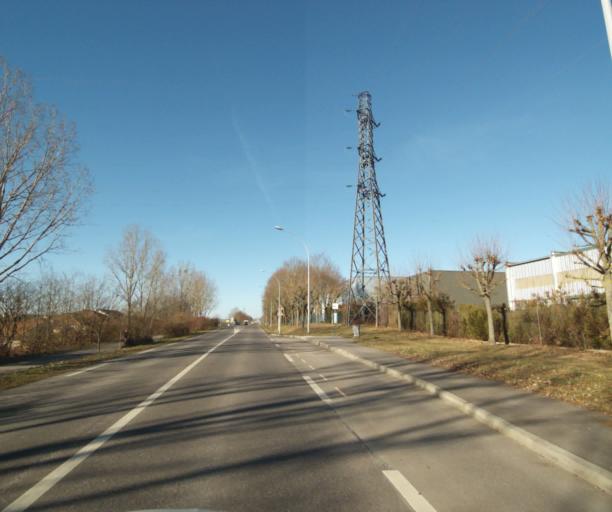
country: FR
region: Lorraine
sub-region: Departement de Meurthe-et-Moselle
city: Heillecourt
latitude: 48.6512
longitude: 6.2080
